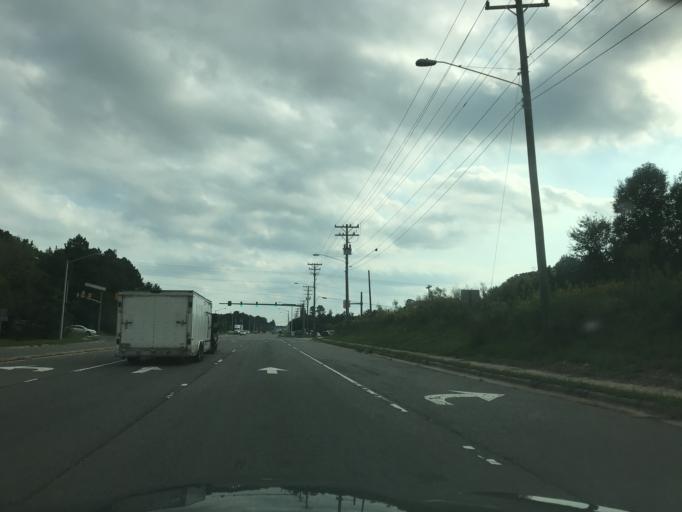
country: US
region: North Carolina
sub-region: Durham County
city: Durham
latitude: 35.9165
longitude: -78.8914
